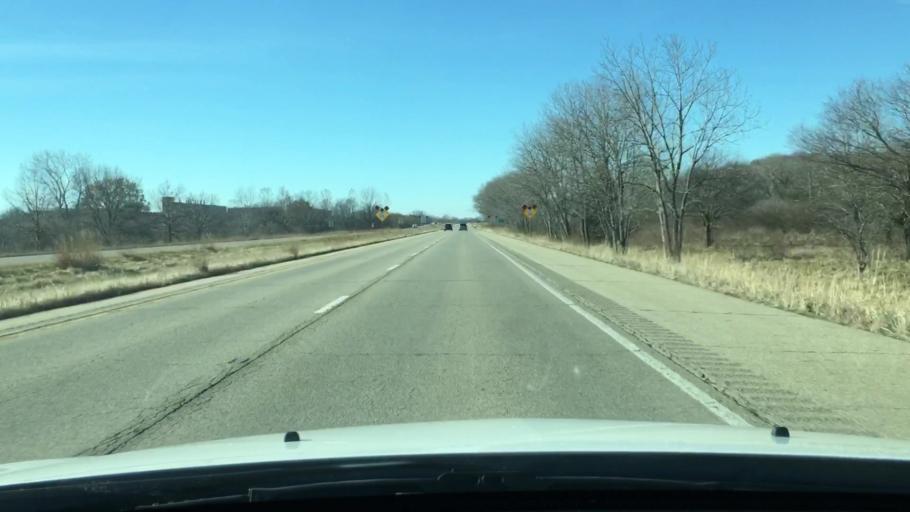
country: US
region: Illinois
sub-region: Peoria County
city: Glasford
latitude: 40.5640
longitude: -89.7387
